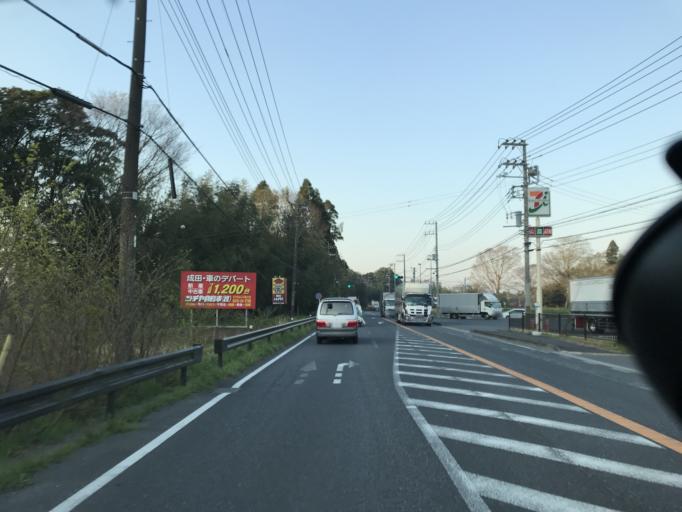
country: JP
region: Chiba
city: Narita
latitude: 35.8019
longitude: 140.3525
